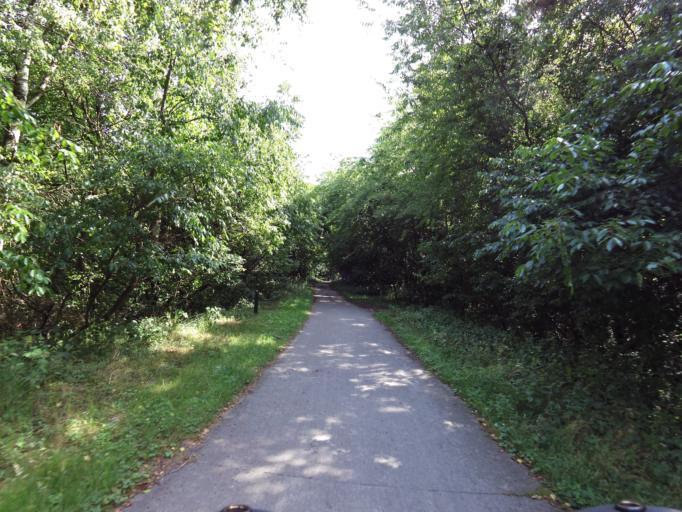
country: NL
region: Zeeland
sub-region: Schouwen-Duiveland
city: Burgh
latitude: 51.6859
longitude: 3.7082
